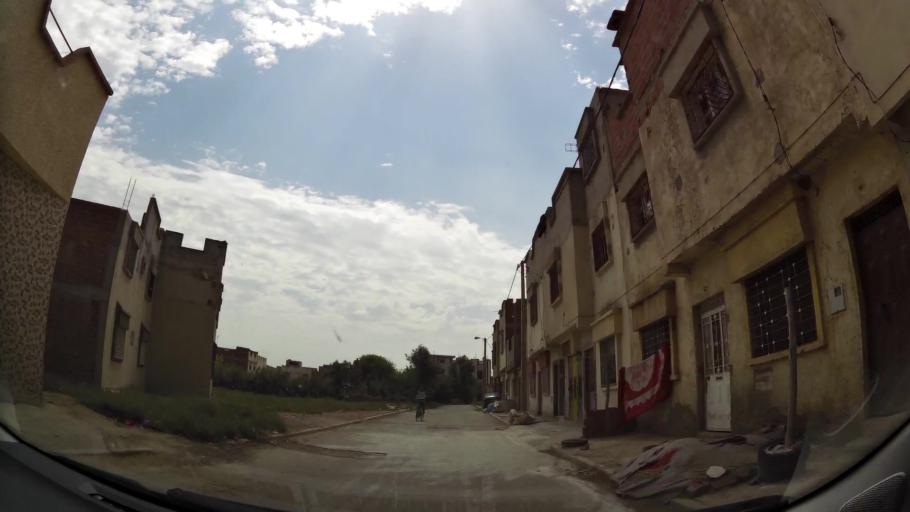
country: MA
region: Oriental
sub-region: Oujda-Angad
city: Oujda
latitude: 34.6825
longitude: -1.8982
